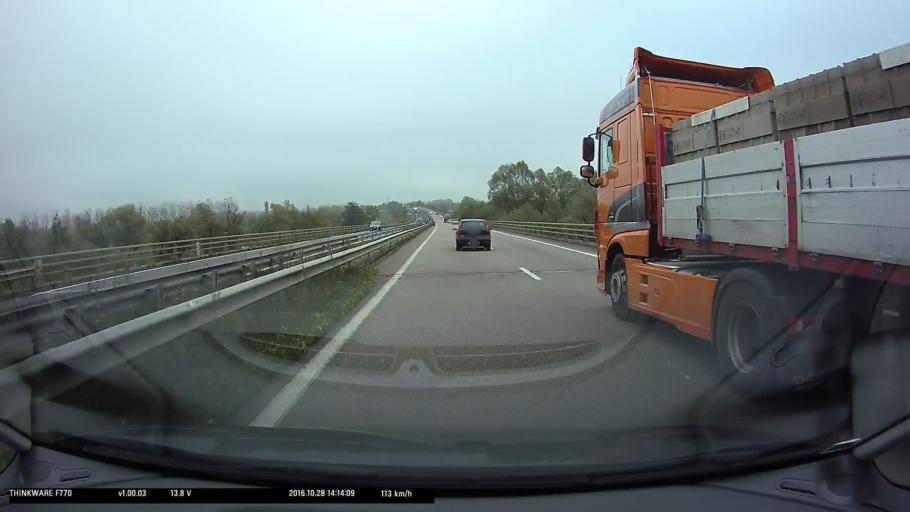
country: FR
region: Lorraine
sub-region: Departement de Meurthe-et-Moselle
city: Luneville
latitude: 48.5784
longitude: 6.4675
